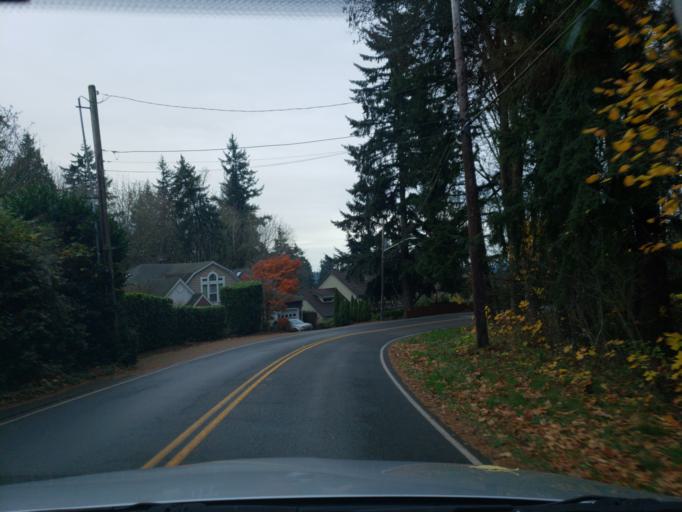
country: US
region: Washington
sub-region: King County
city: Bothell
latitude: 47.7434
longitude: -122.2013
